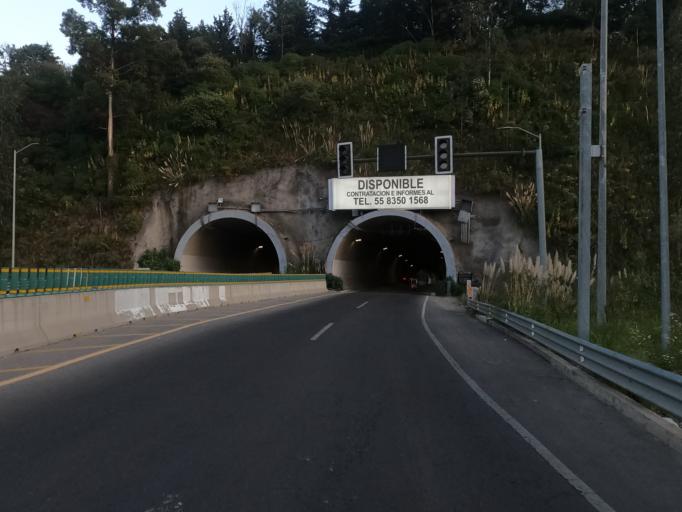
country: MX
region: Mexico
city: San Bartolome Coatepec
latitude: 19.4122
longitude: -99.2838
